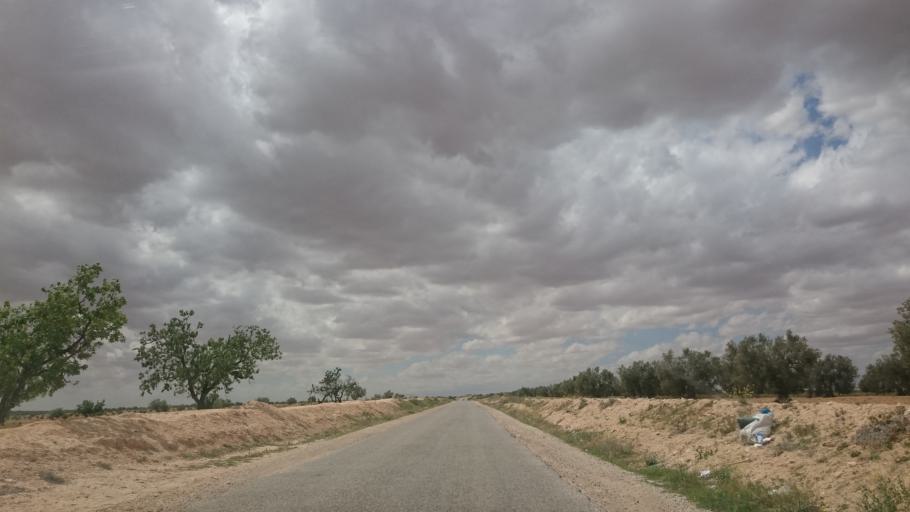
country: TN
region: Safaqis
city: Sfax
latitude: 34.7495
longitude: 10.5032
